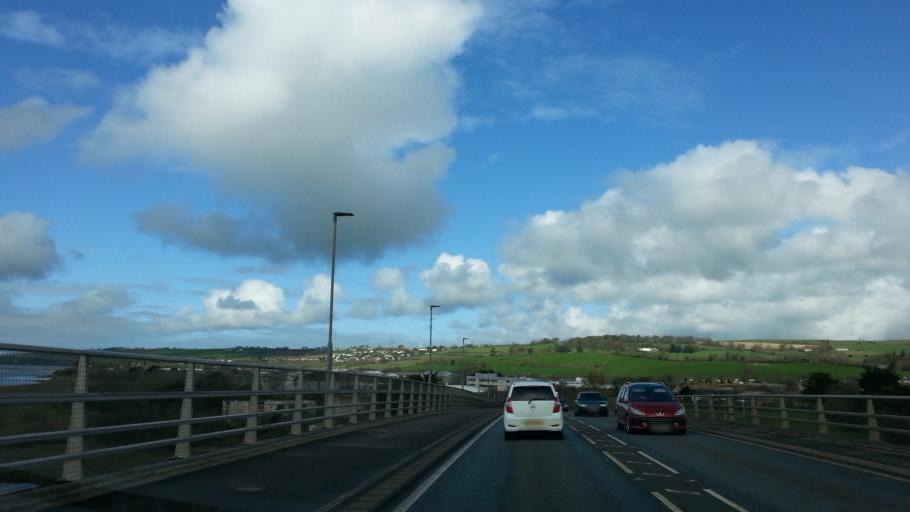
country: GB
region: England
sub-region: Devon
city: Barnstaple
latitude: 51.0800
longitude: -4.0710
